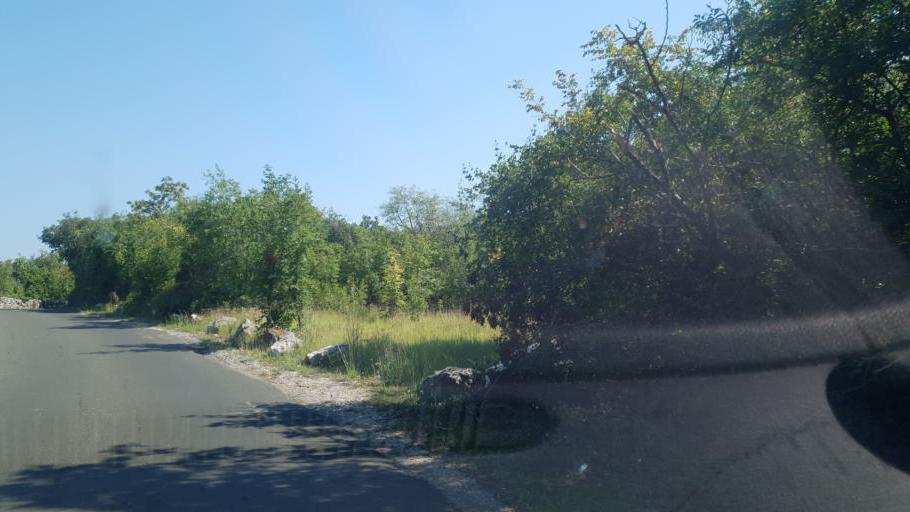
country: HR
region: Primorsko-Goranska
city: Omisalj
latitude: 45.1677
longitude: 14.5974
